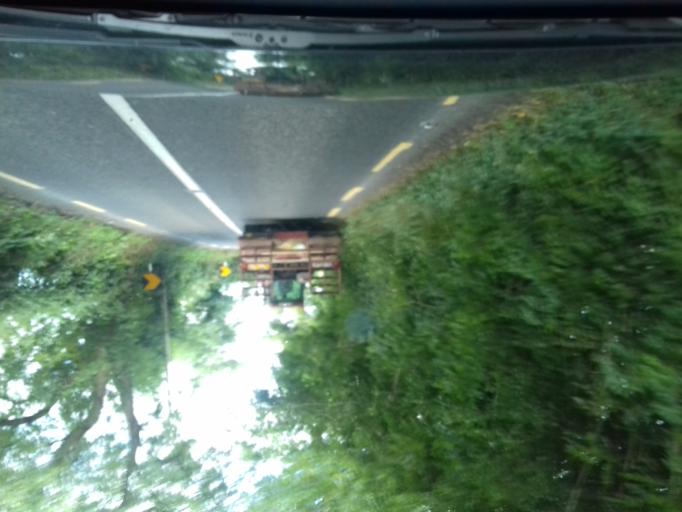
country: IE
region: Leinster
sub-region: County Carlow
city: Tullow
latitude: 52.8313
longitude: -6.7188
